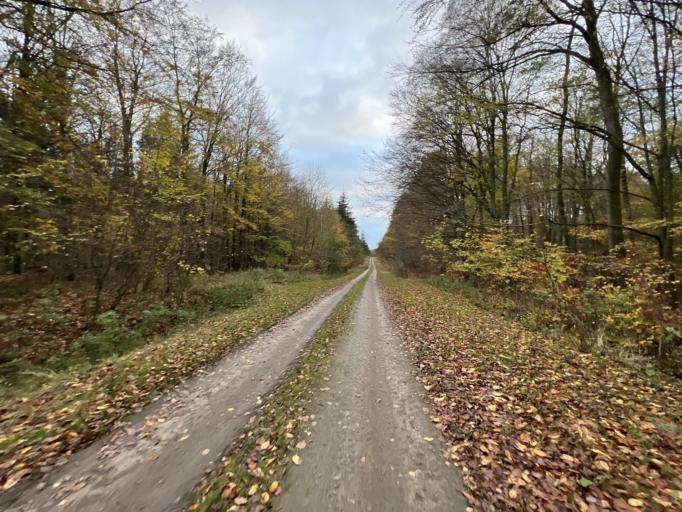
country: DE
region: Mecklenburg-Vorpommern
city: Putbus
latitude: 54.3696
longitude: 13.4542
